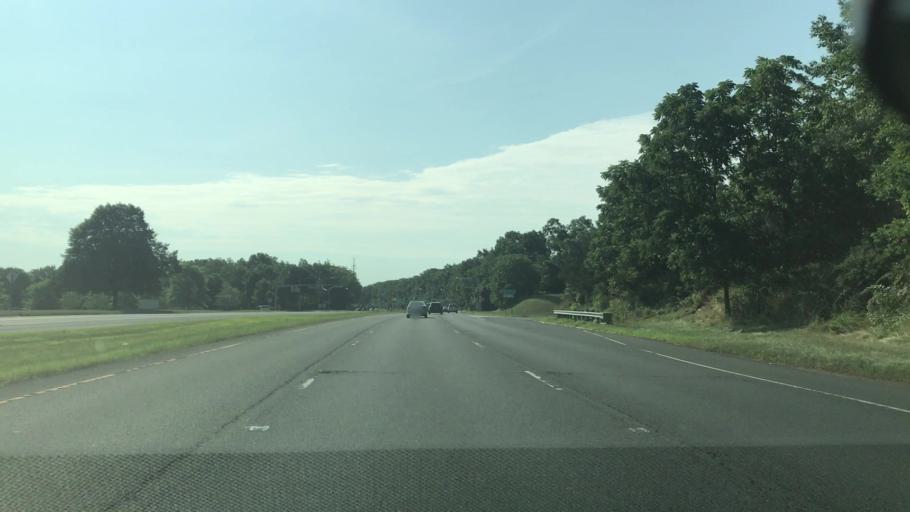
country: US
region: New Jersey
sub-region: Somerset County
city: Raritan
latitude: 40.5862
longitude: -74.6344
